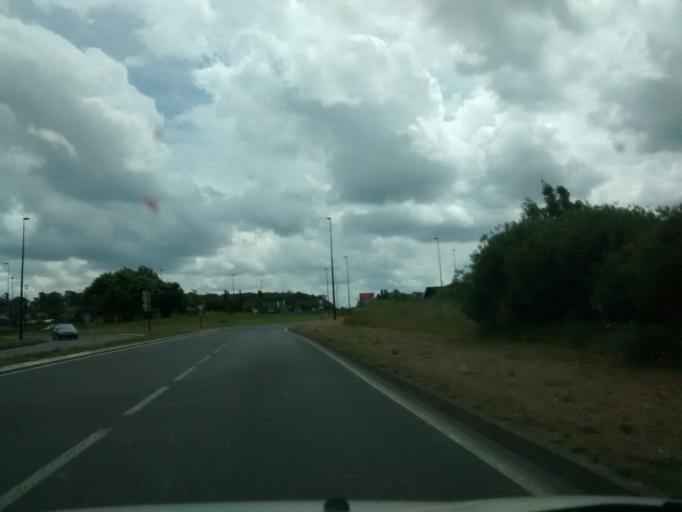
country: FR
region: Brittany
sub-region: Departement des Cotes-d'Armor
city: Lannion
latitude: 48.7361
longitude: -3.4377
